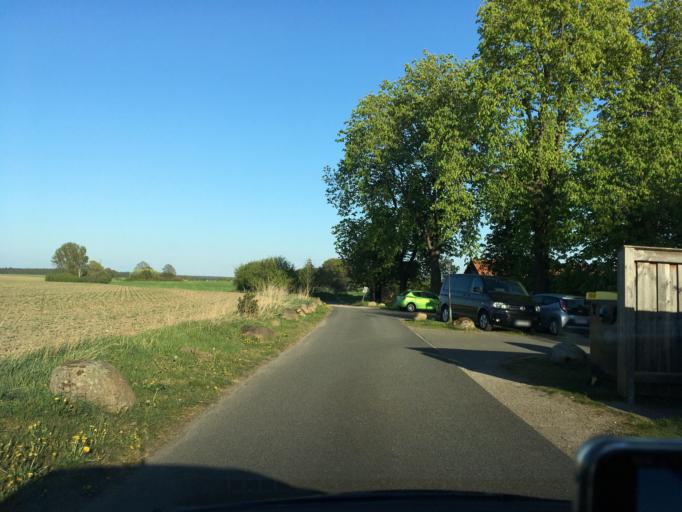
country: DE
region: Lower Saxony
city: Wendisch Evern
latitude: 53.2246
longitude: 10.4604
